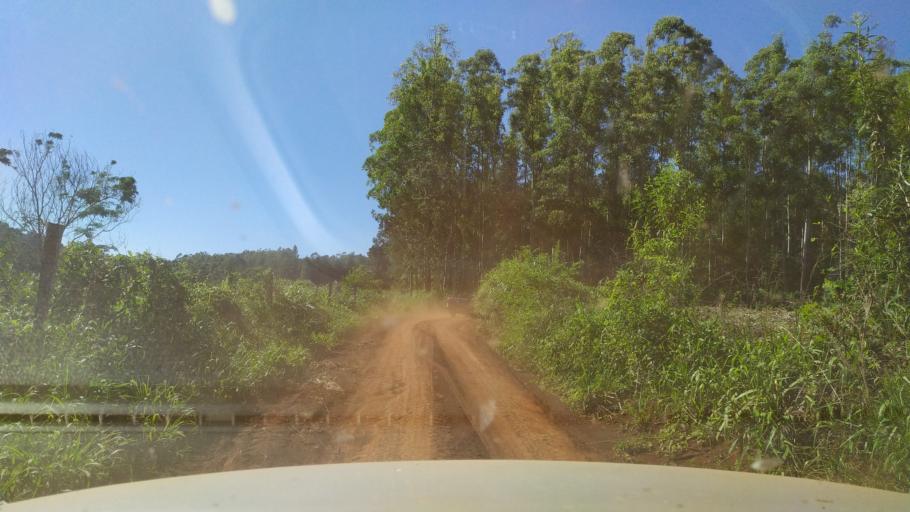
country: AR
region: Misiones
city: Caraguatay
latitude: -26.6718
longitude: -54.6970
